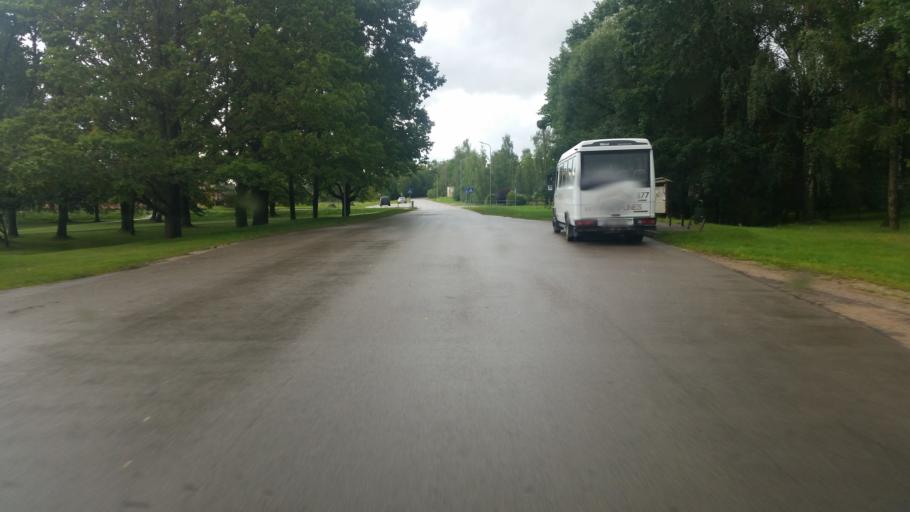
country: LV
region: Vecumnieki
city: Vecumnieki
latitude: 56.4324
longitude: 24.4631
